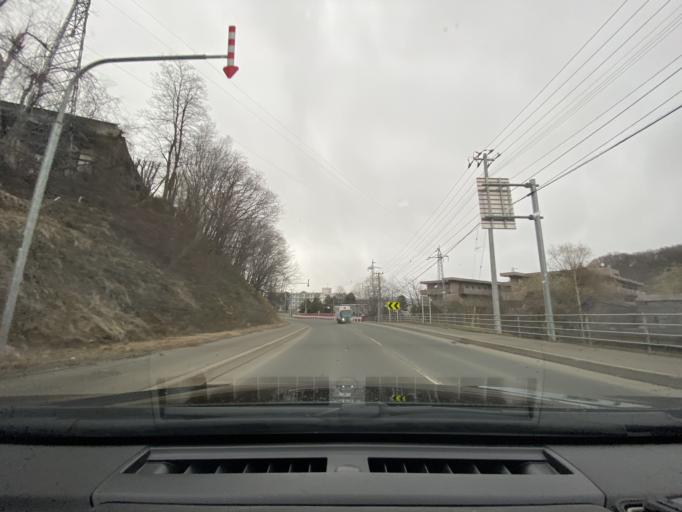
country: JP
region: Hokkaido
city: Kitami
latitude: 43.7964
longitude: 143.9168
